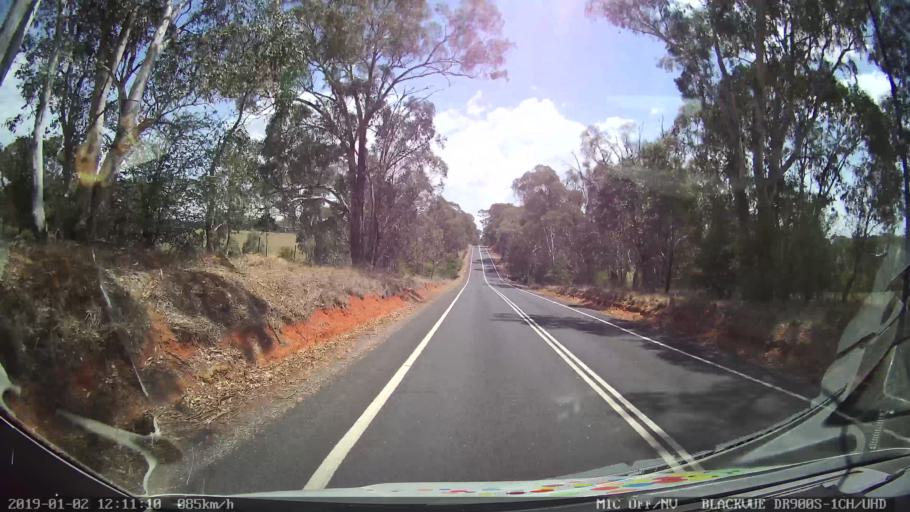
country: AU
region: New South Wales
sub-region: Young
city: Young
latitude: -34.4524
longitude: 148.2584
